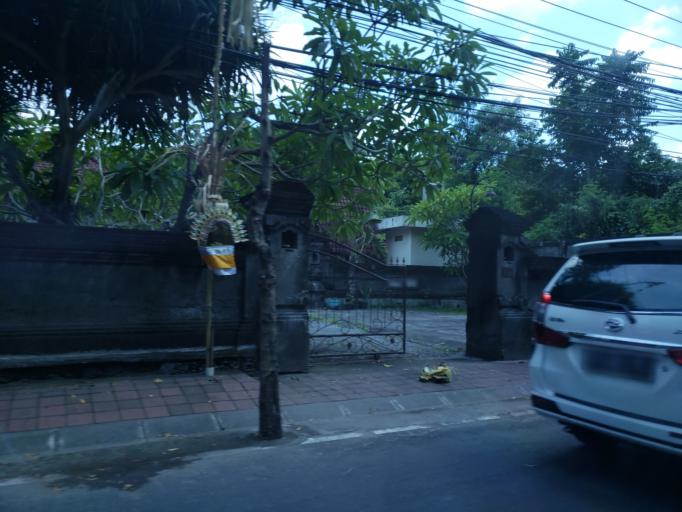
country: ID
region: Bali
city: Jimbaran
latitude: -8.7805
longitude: 115.1678
